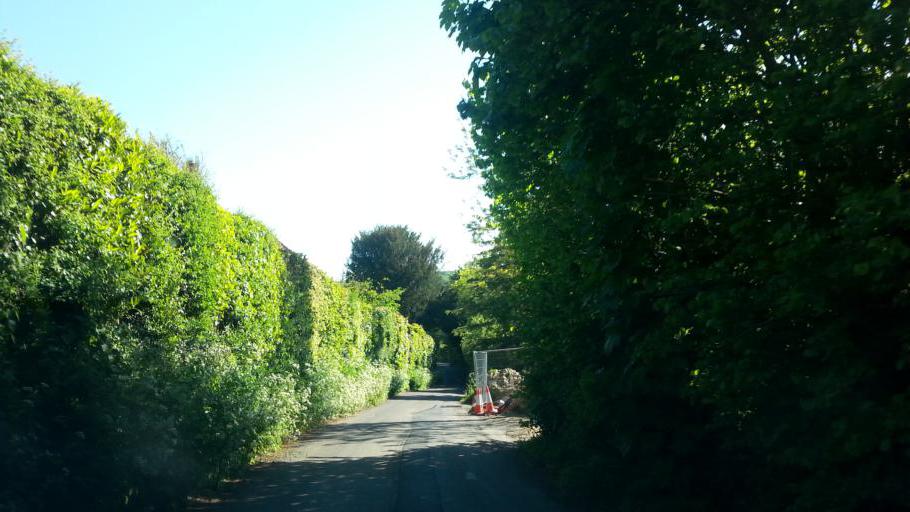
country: GB
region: England
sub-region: Somerset
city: Milborne Port
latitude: 50.9734
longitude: -2.4620
